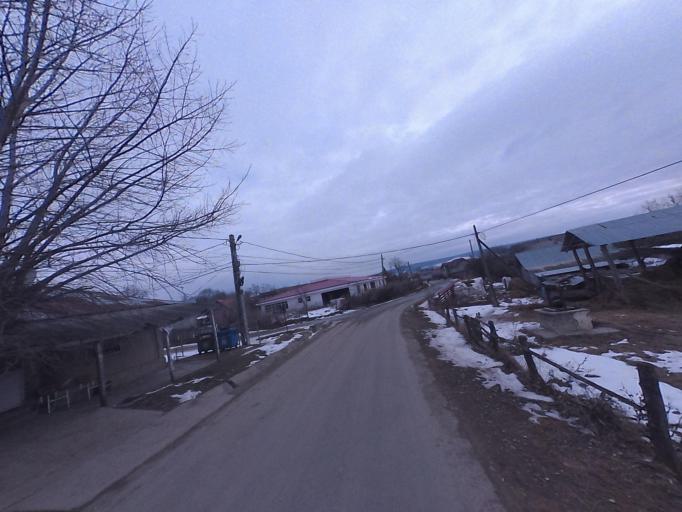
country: RO
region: Iasi
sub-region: Comuna Tibanesti
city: Glodenii Gandului
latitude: 46.9781
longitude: 27.2929
